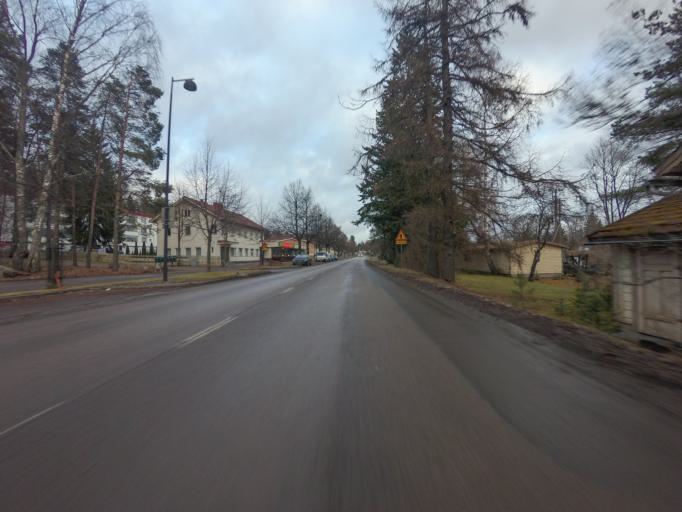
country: FI
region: Uusimaa
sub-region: Helsinki
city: Lohja
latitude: 60.2660
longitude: 24.1166
